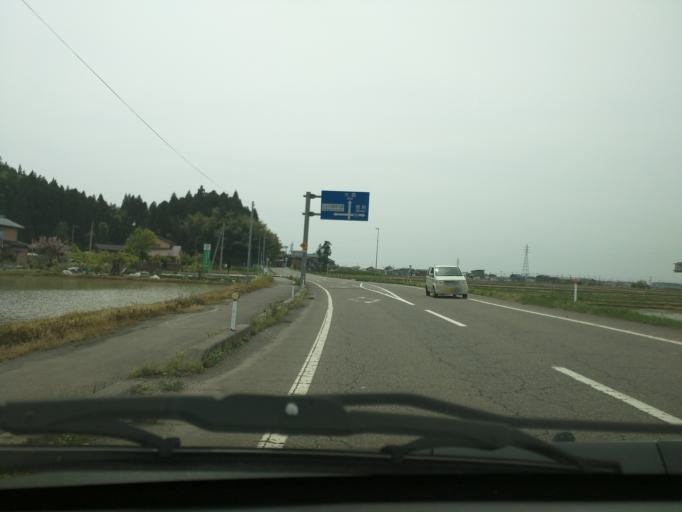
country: JP
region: Niigata
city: Mitsuke
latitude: 37.5737
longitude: 138.9461
